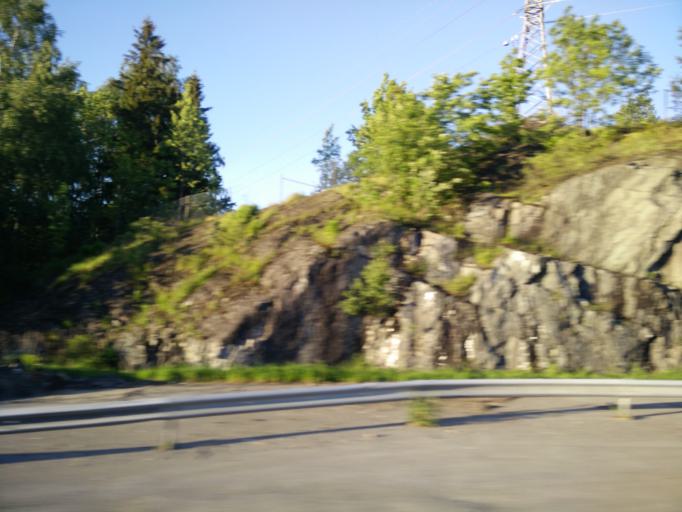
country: NO
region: Akershus
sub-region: Asker
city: Billingstad
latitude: 59.9047
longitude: 10.4917
